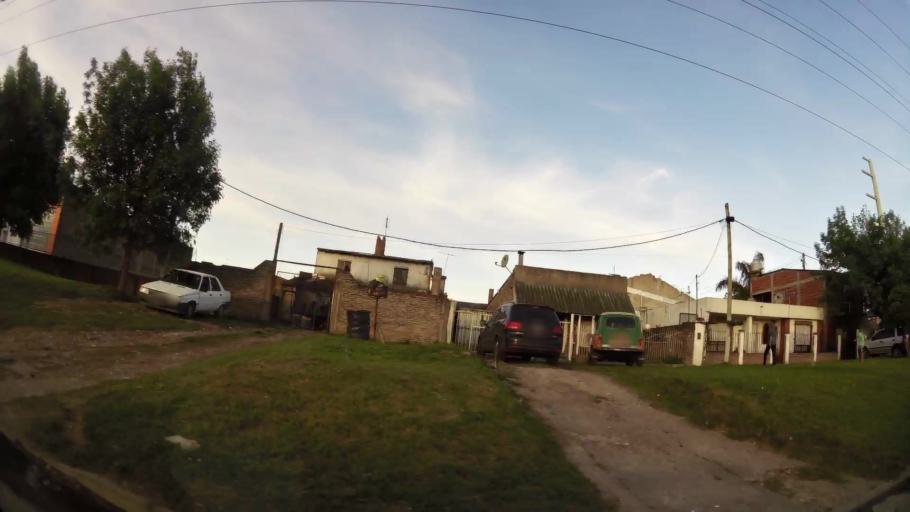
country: AR
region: Buenos Aires
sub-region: Partido de Quilmes
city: Quilmes
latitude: -34.7804
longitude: -58.2250
